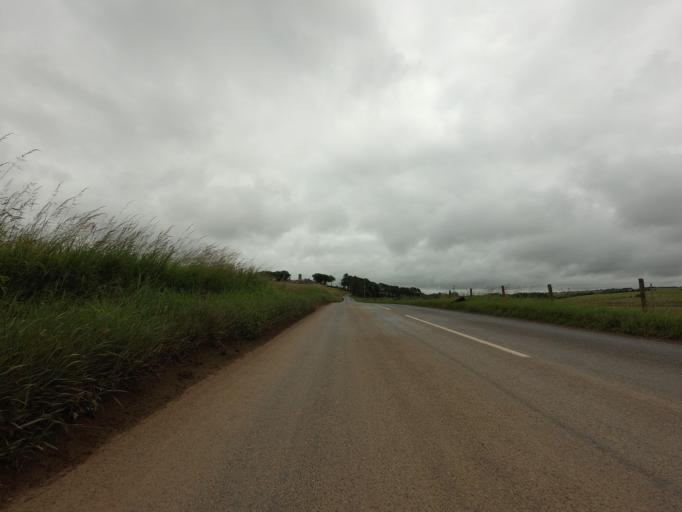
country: GB
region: Scotland
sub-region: Aberdeenshire
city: Turriff
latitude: 57.5426
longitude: -2.3617
